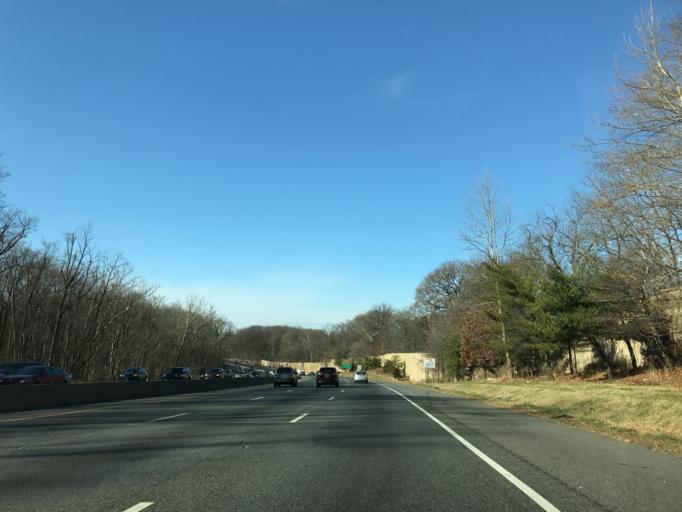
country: US
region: Maryland
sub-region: Baltimore County
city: Hampton
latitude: 39.4138
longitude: -76.5868
